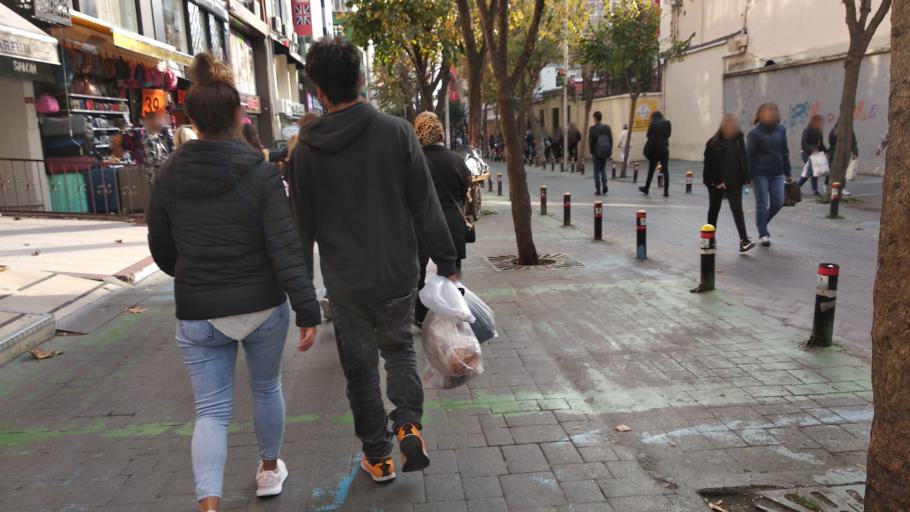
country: TR
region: Istanbul
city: Bahcelievler
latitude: 40.9772
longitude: 28.8749
